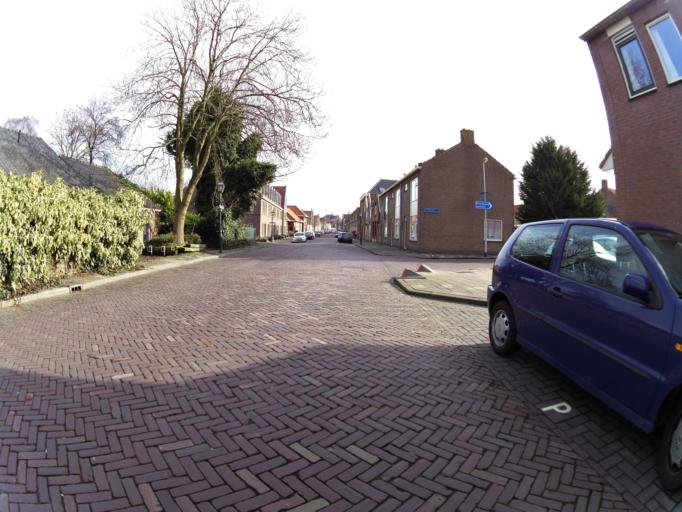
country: NL
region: South Holland
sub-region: Gemeente Brielle
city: Brielle
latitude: 51.9048
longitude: 4.1609
